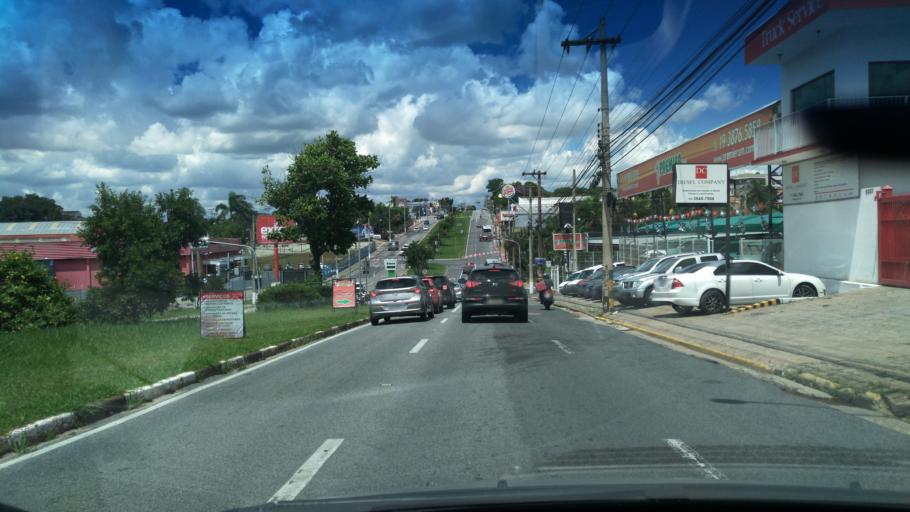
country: BR
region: Sao Paulo
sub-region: Vinhedo
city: Vinhedo
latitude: -23.0238
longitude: -46.9829
